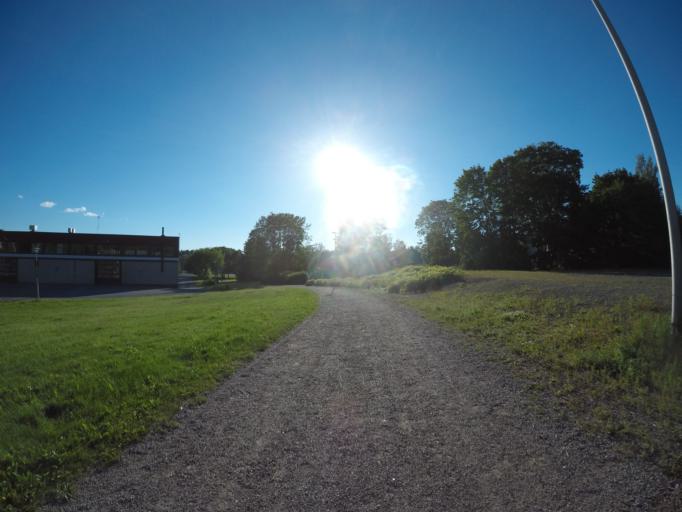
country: FI
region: Haeme
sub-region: Haemeenlinna
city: Haemeenlinna
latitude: 60.9884
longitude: 24.4467
